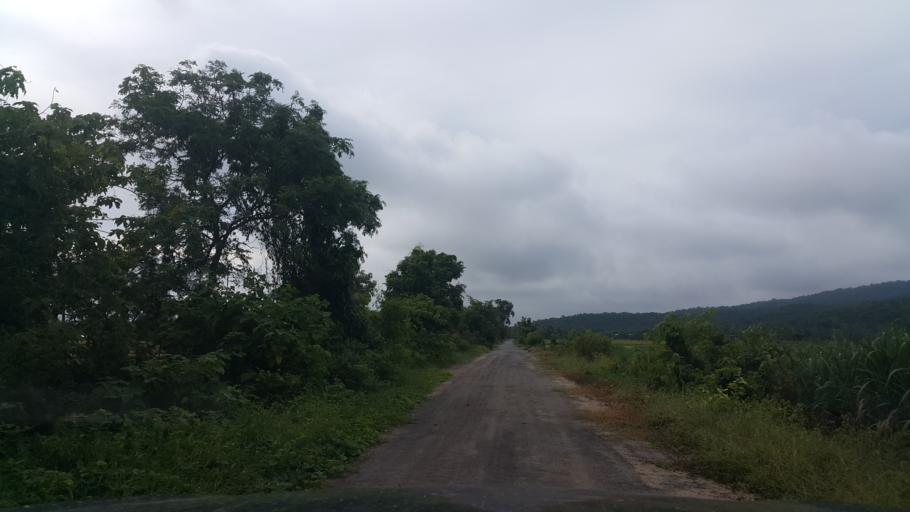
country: TH
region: Sukhothai
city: Sawankhalok
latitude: 17.3100
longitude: 99.6983
